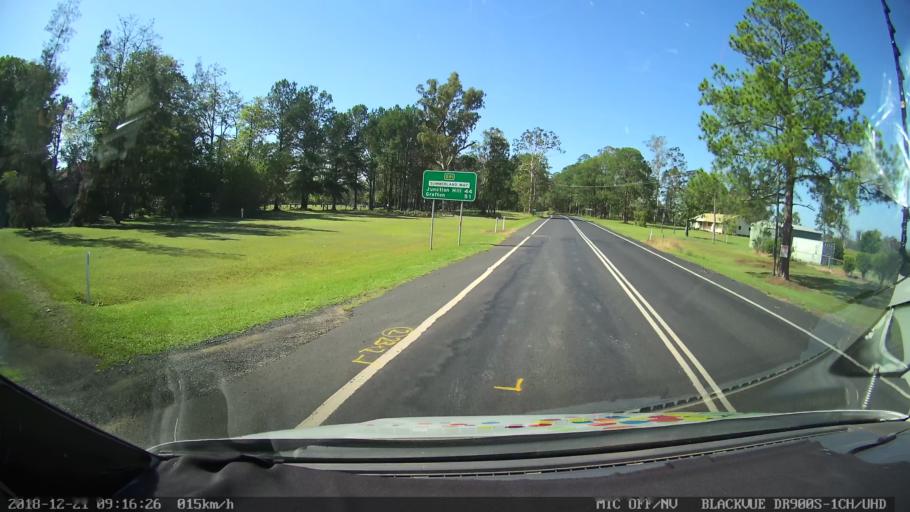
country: AU
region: New South Wales
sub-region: Clarence Valley
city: Maclean
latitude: -29.2829
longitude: 152.9893
